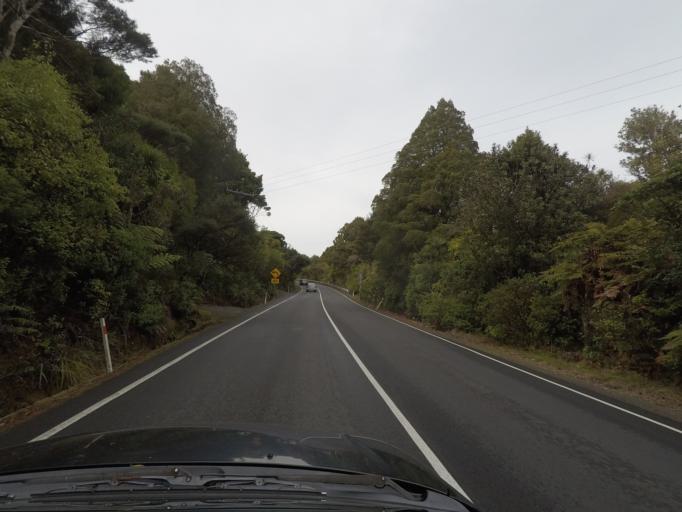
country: NZ
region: Auckland
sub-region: Auckland
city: Titirangi
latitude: -36.9479
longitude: 174.5220
